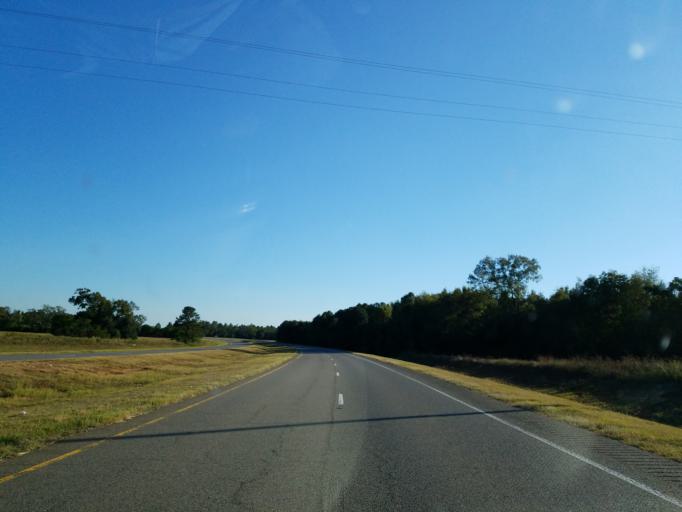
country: US
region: Georgia
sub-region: Lee County
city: Leesburg
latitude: 31.7326
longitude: -84.1823
